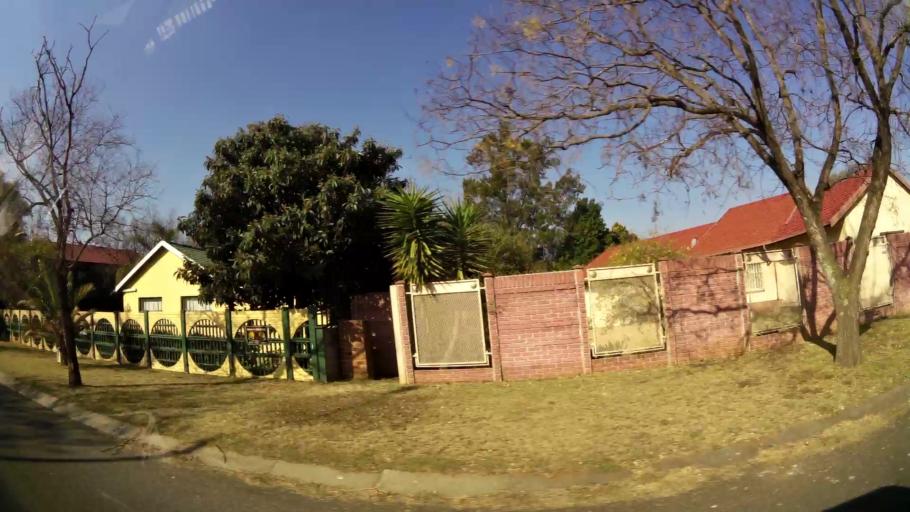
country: ZA
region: Gauteng
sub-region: West Rand District Municipality
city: Randfontein
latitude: -26.1756
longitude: 27.6896
